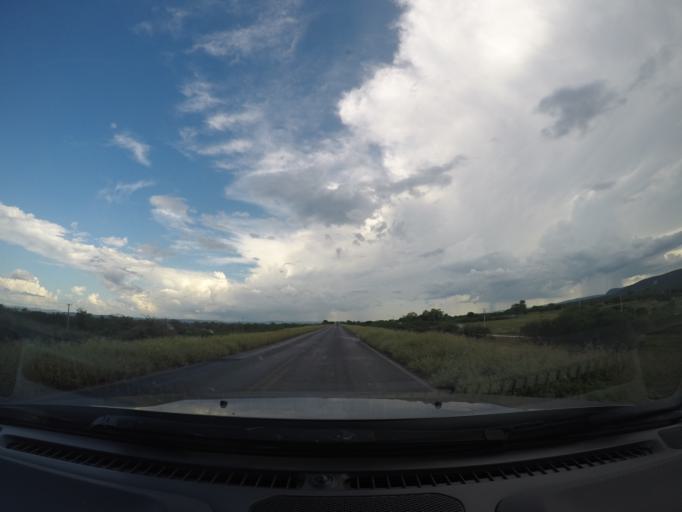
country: BR
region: Bahia
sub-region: Ibotirama
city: Ibotirama
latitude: -12.1460
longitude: -43.3149
